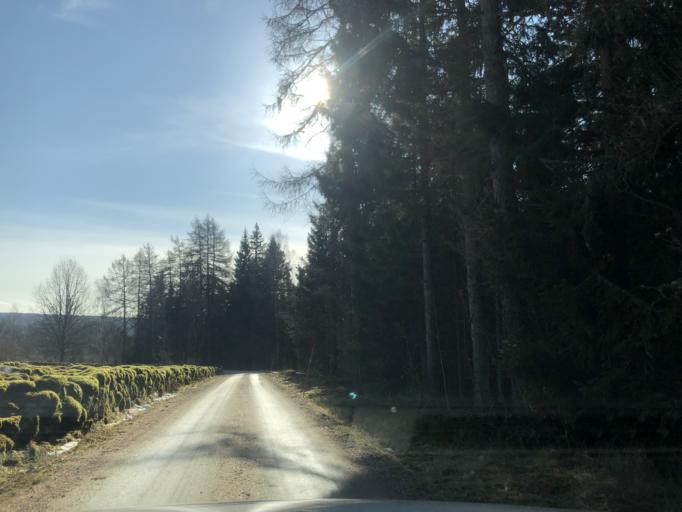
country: SE
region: Vaestra Goetaland
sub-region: Ulricehamns Kommun
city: Ulricehamn
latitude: 57.8081
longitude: 13.3855
